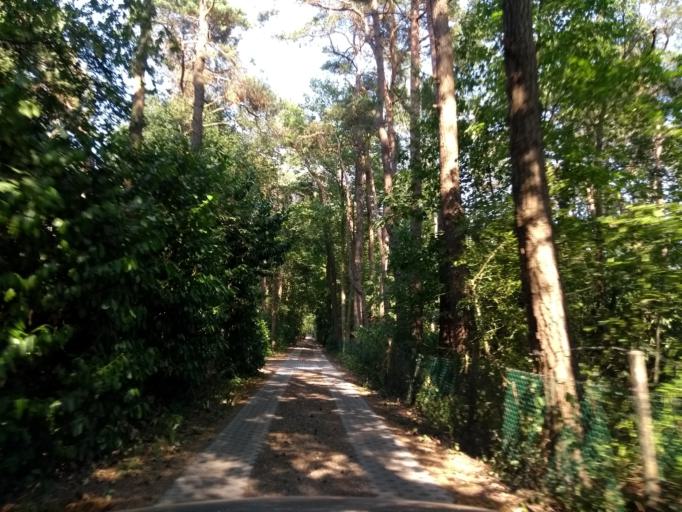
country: NL
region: Overijssel
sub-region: Gemeente Almelo
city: Almelo
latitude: 52.3258
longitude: 6.6804
